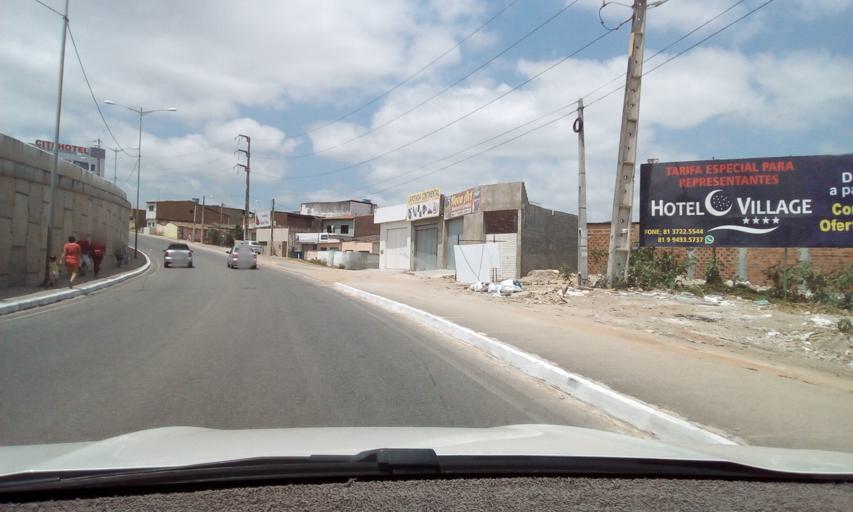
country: BR
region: Pernambuco
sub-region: Caruaru
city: Caruaru
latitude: -8.2839
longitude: -35.9833
